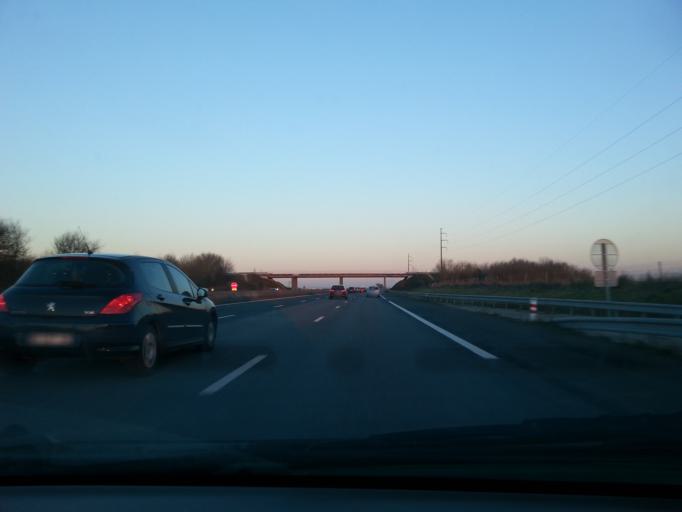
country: FR
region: Centre
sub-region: Departement d'Eure-et-Loir
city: Bailleau-le-Pin
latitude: 48.3135
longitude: 1.3192
